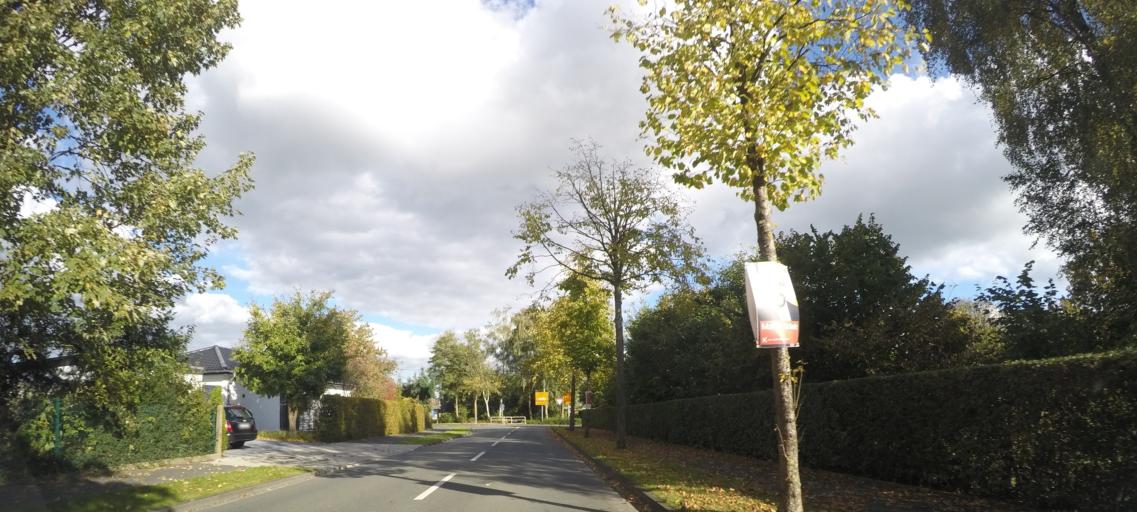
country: DE
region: North Rhine-Westphalia
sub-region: Regierungsbezirk Munster
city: Wadersloh
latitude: 51.7078
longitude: 8.2535
